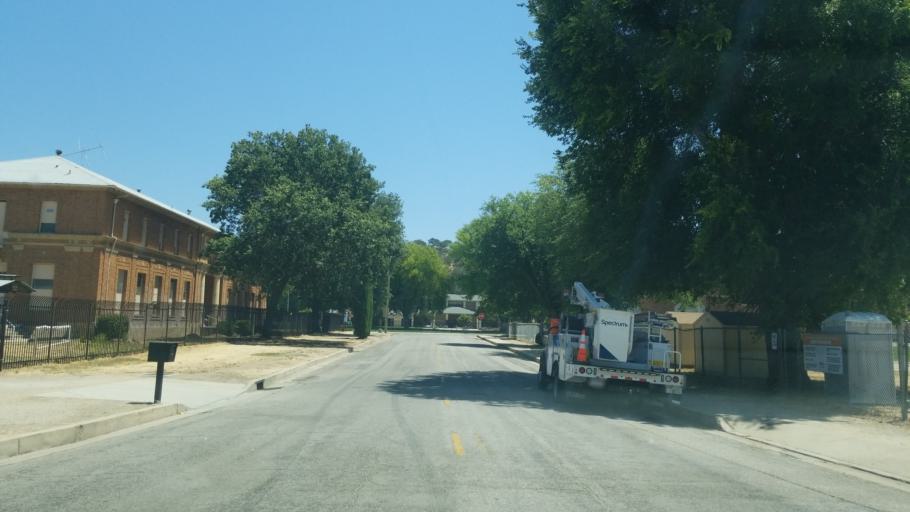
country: US
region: California
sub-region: San Luis Obispo County
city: Atascadero
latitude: 35.4922
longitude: -120.6674
